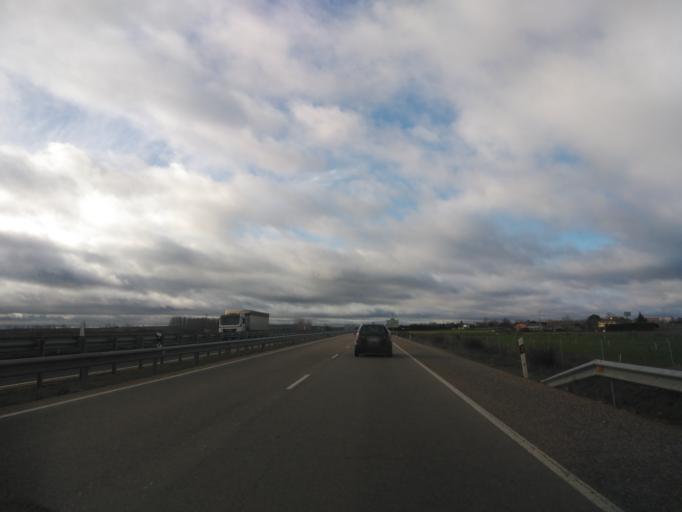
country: ES
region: Castille and Leon
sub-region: Provincia de Zamora
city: Zamora
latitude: 41.4900
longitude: -5.7356
